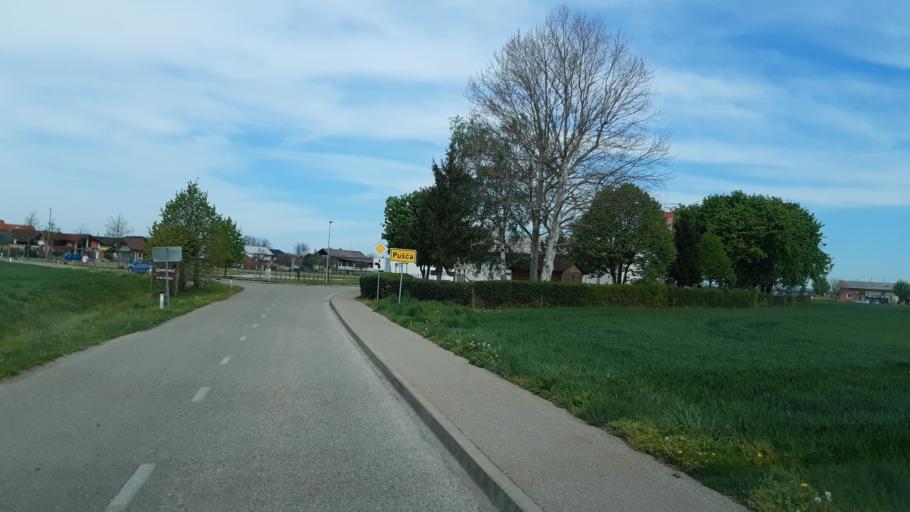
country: SI
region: Murska Sobota
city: Krog
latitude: 46.6530
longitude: 16.1417
